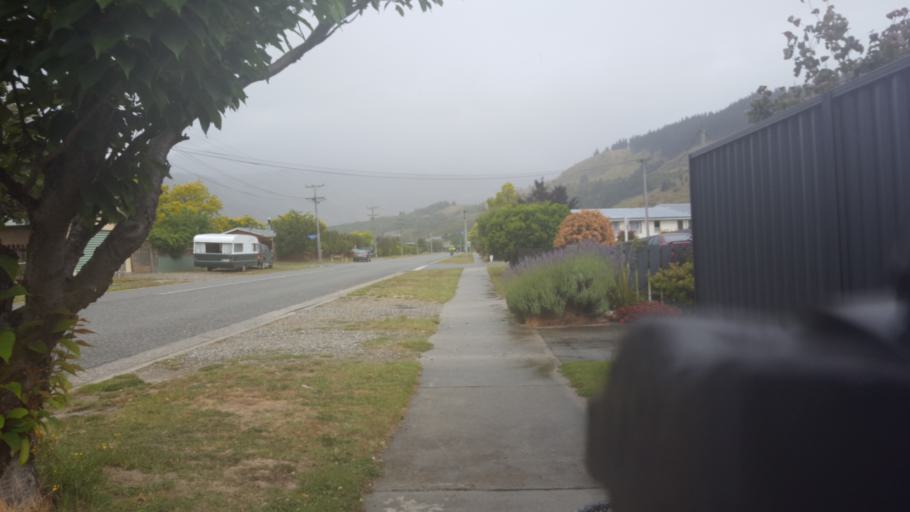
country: NZ
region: Otago
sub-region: Queenstown-Lakes District
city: Wanaka
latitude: -45.1900
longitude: 169.3271
